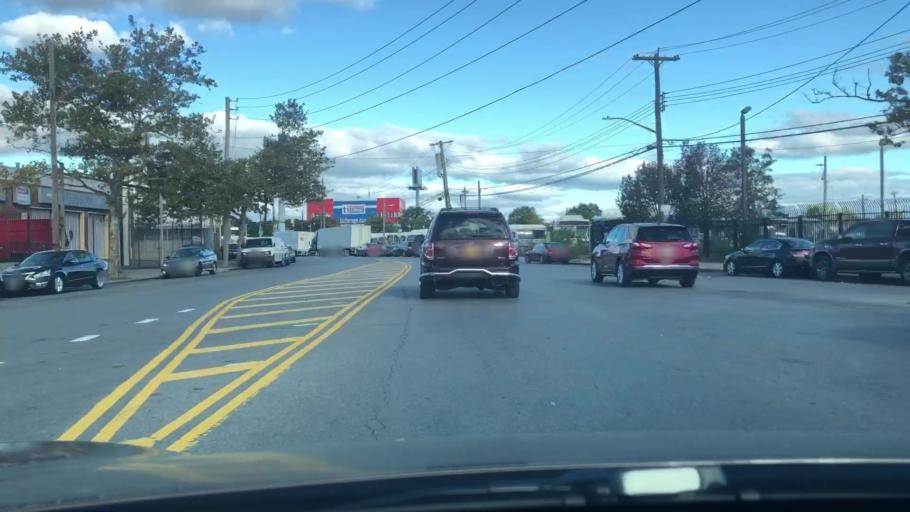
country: US
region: New York
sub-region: Bronx
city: Eastchester
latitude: 40.8821
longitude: -73.8234
